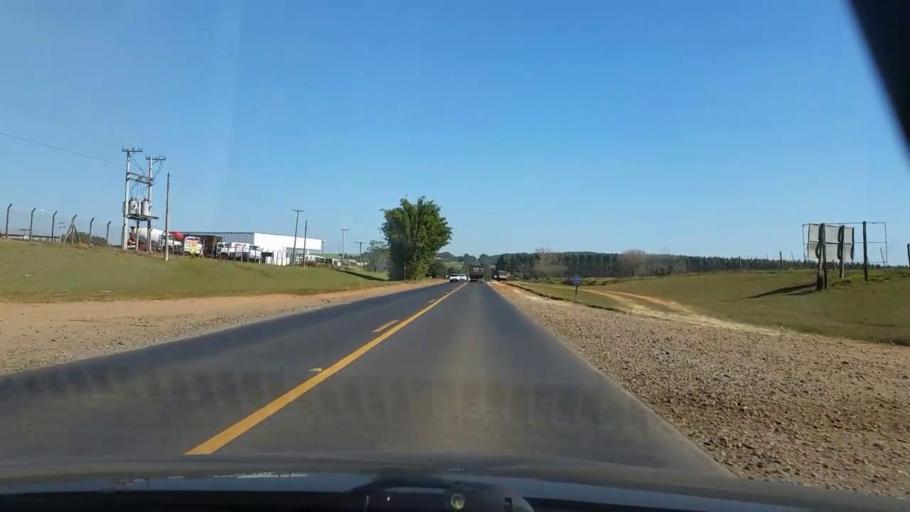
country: BR
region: Sao Paulo
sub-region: Sao Manuel
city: Sao Manuel
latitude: -22.8023
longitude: -48.6670
